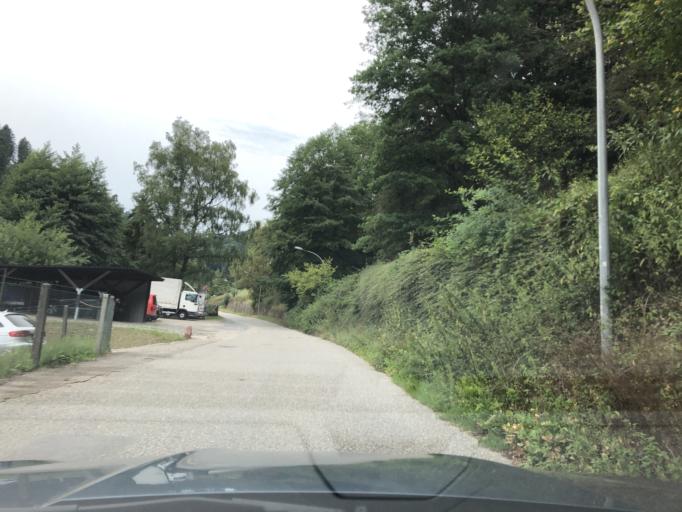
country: DE
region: Baden-Wuerttemberg
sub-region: Karlsruhe Region
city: Schonau
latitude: 49.4334
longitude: 8.8046
